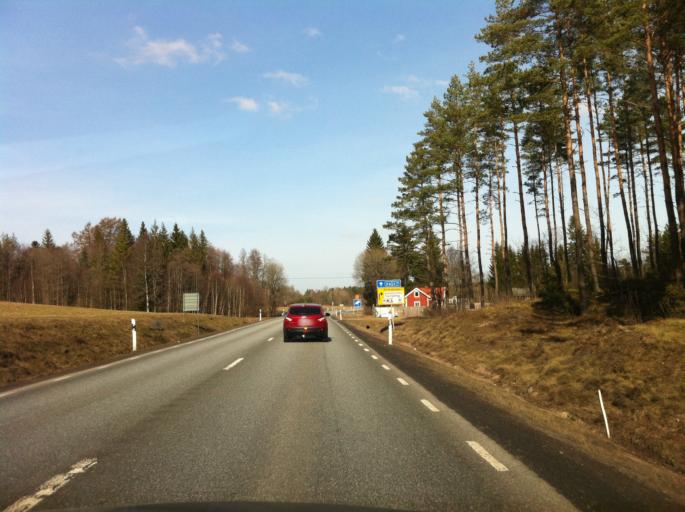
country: SE
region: Joenkoeping
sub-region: Mullsjo Kommun
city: Mullsjoe
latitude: 57.9889
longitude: 13.8286
